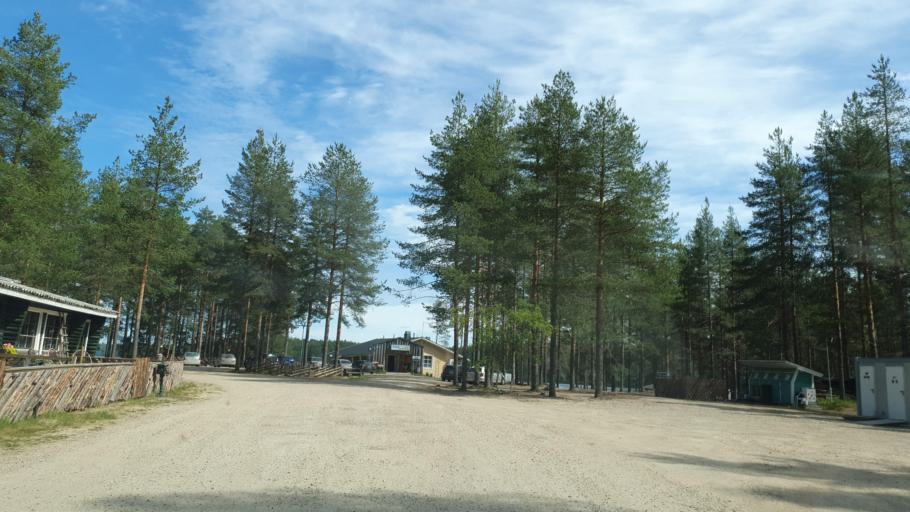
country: FI
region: Kainuu
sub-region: Kehys-Kainuu
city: Hyrynsalmi
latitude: 64.6948
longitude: 28.4914
